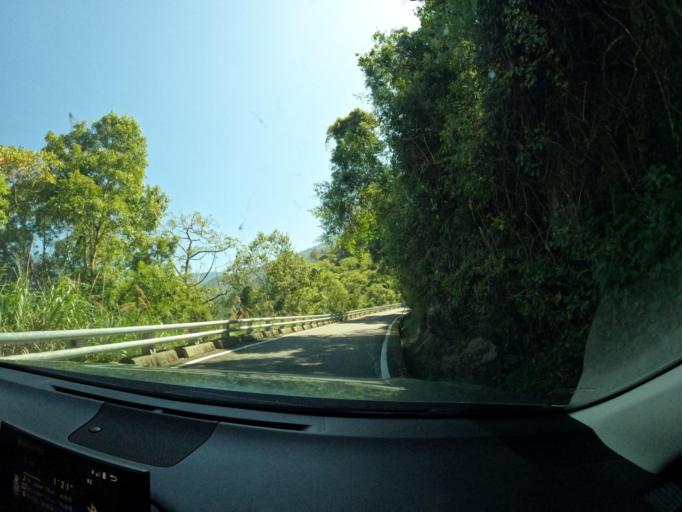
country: TW
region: Taiwan
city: Yujing
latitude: 23.2882
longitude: 120.8582
